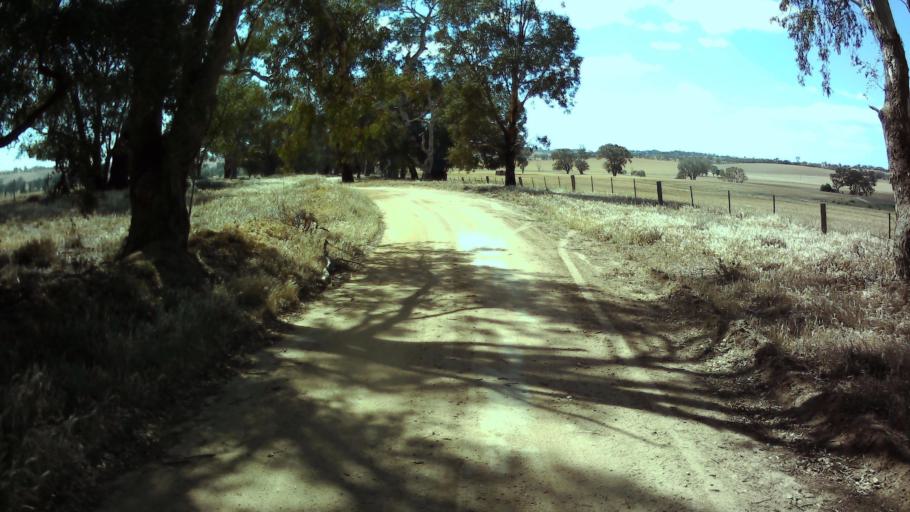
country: AU
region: New South Wales
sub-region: Weddin
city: Grenfell
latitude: -33.9562
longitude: 148.4253
